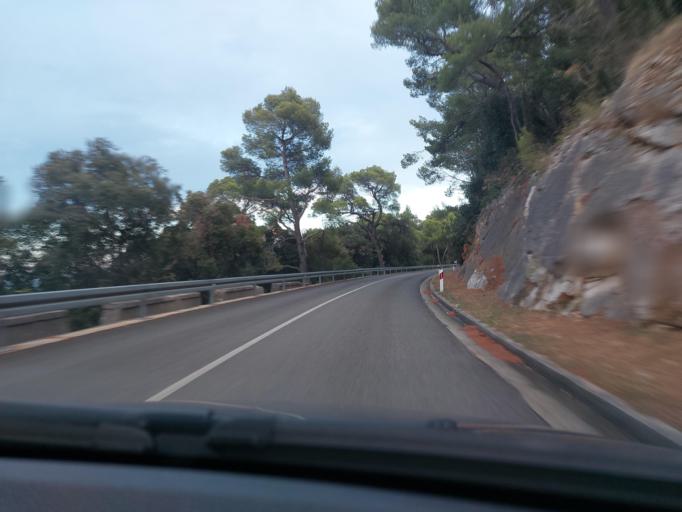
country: HR
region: Dubrovacko-Neretvanska
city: Smokvica
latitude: 42.7685
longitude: 16.8799
